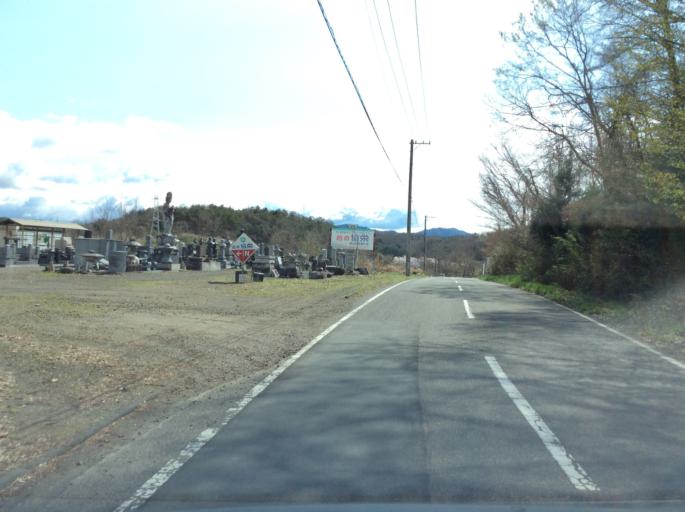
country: JP
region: Fukushima
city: Koriyama
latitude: 37.3523
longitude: 140.4215
